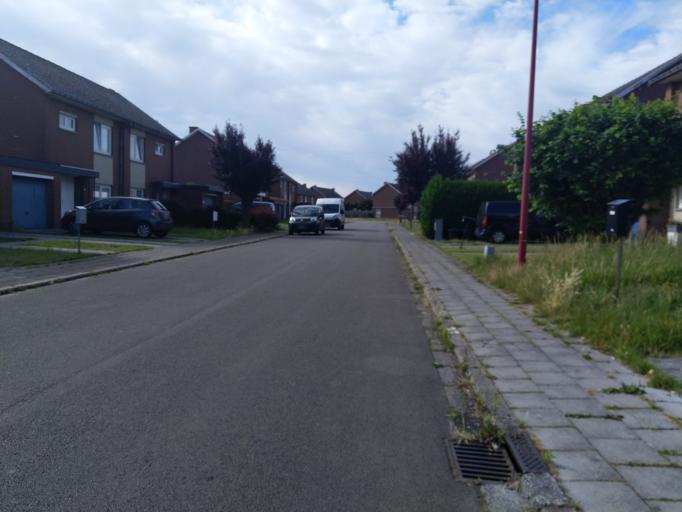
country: BE
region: Wallonia
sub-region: Province du Hainaut
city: Quaregnon
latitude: 50.4465
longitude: 3.8520
